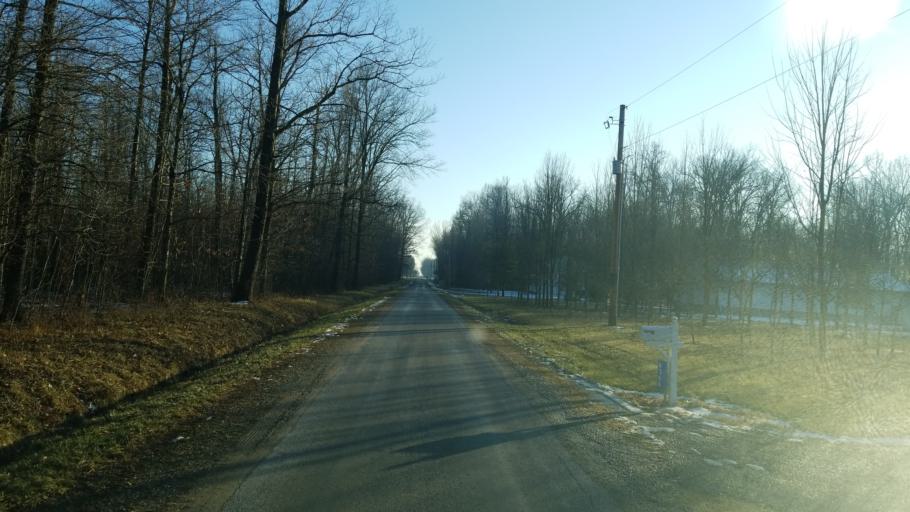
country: US
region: Ohio
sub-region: Crawford County
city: Bucyrus
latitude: 40.9355
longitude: -82.9210
